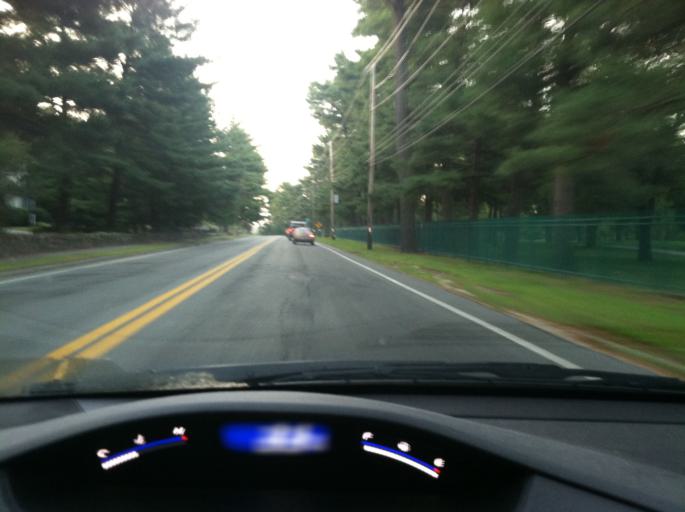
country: US
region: Massachusetts
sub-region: Middlesex County
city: Bedford
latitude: 42.4790
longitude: -71.2550
